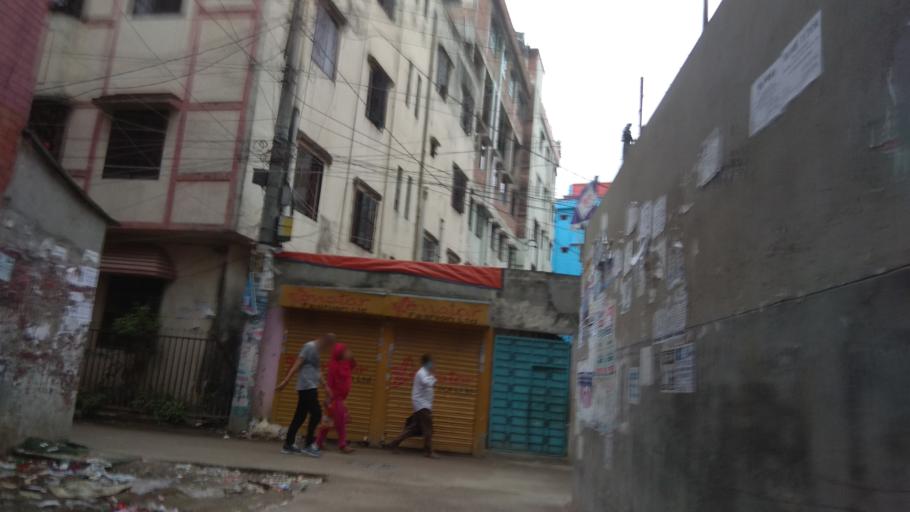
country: BD
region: Dhaka
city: Azimpur
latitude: 23.7974
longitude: 90.3840
